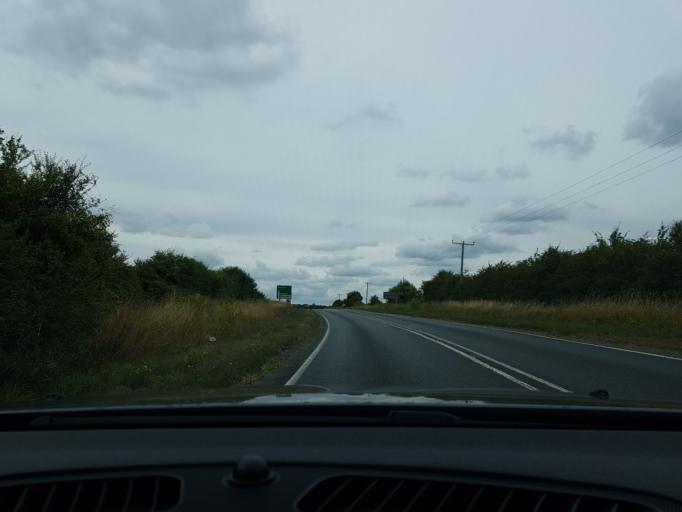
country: GB
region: England
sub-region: Hampshire
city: Basingstoke
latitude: 51.2873
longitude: -1.1410
